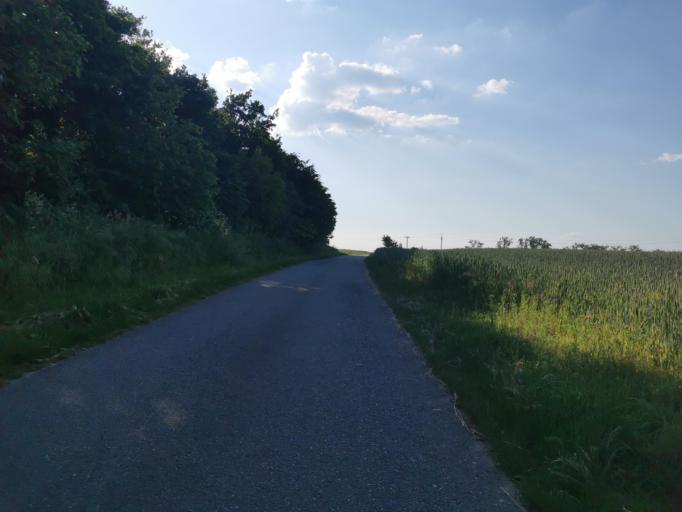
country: CZ
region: South Moravian
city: Straznice
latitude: 48.8837
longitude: 17.3437
